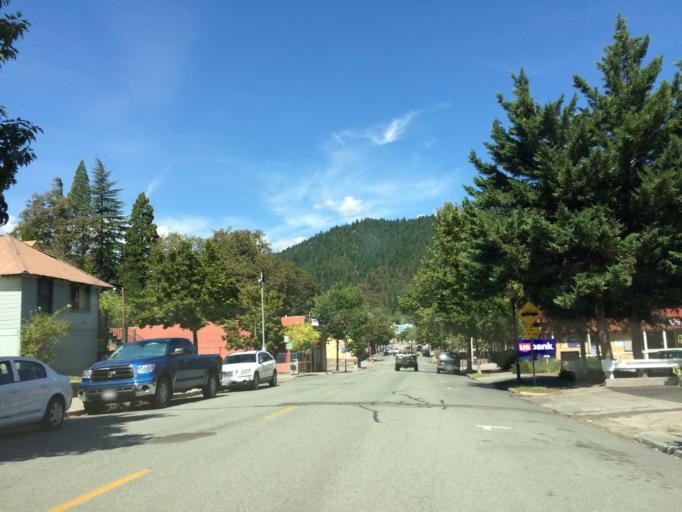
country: US
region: California
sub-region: Siskiyou County
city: Dunsmuir
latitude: 41.2091
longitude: -122.2732
